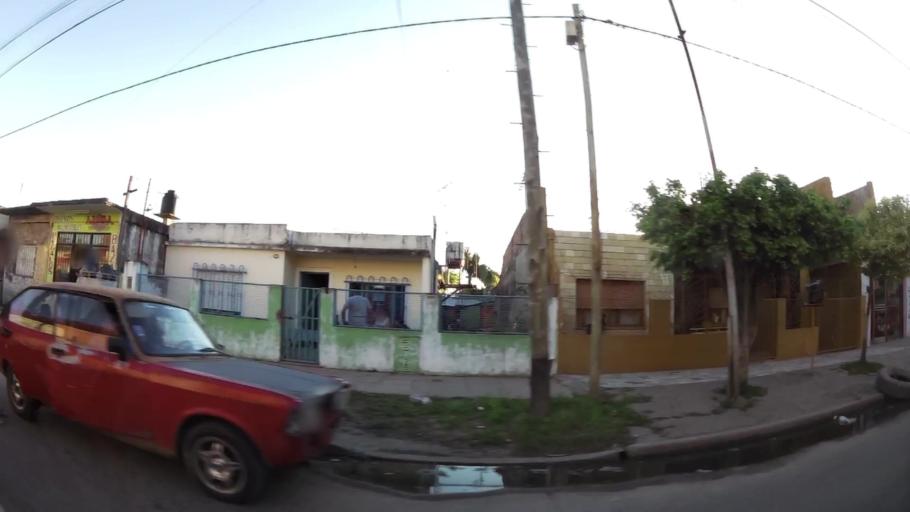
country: AR
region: Buenos Aires
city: San Justo
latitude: -34.7301
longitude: -58.6116
